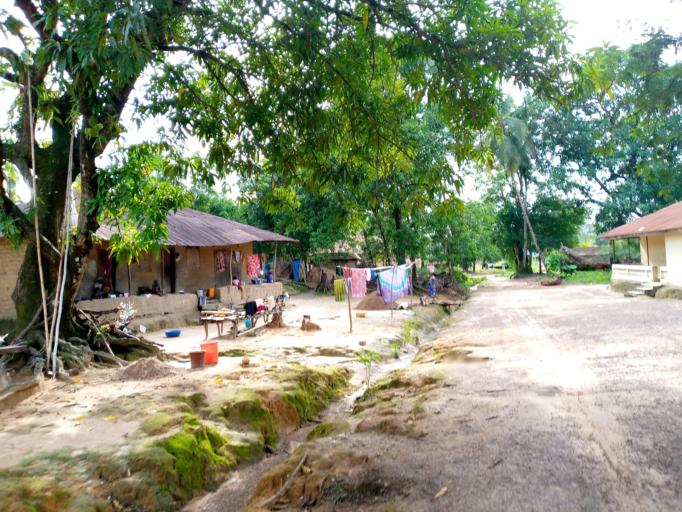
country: SL
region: Northern Province
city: Magburaka
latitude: 8.7184
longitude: -11.9504
